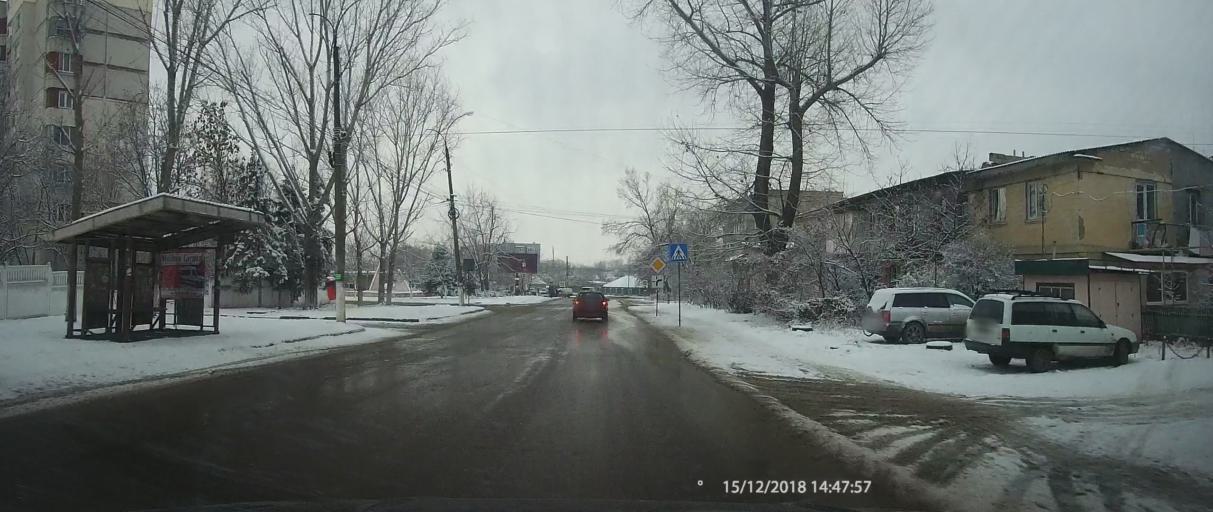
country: MD
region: Cahul
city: Cahul
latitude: 45.8957
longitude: 28.2008
